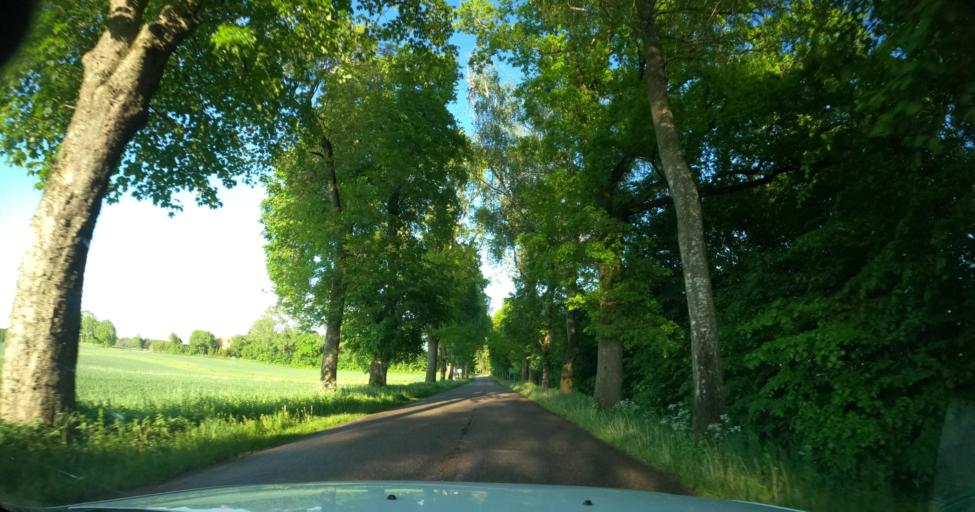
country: PL
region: Warmian-Masurian Voivodeship
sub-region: Powiat braniewski
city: Pieniezno
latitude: 54.2545
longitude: 19.9772
